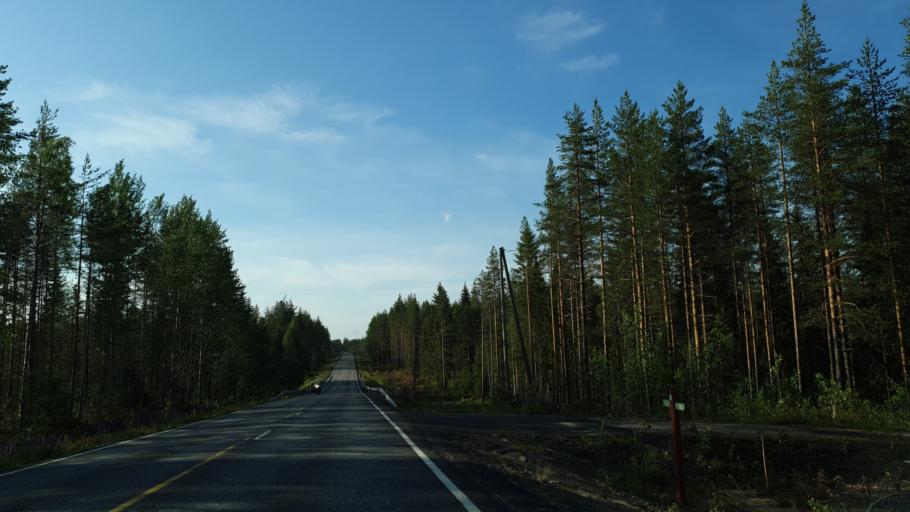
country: FI
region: Kainuu
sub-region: Kehys-Kainuu
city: Kuhmo
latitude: 64.0858
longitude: 29.4834
